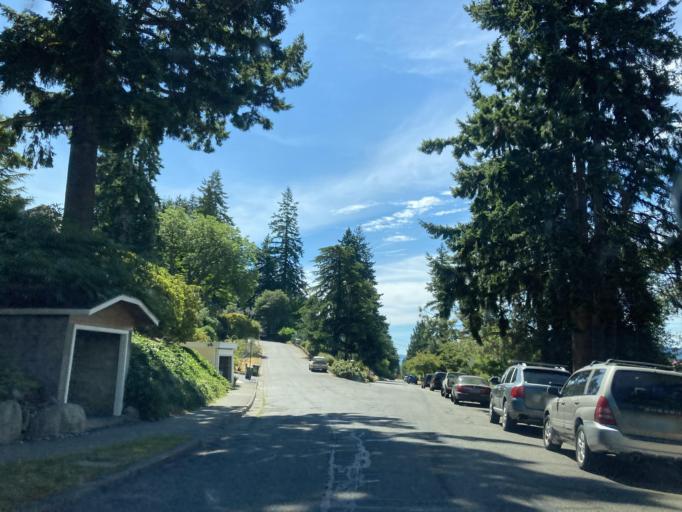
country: US
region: Washington
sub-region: Whatcom County
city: Bellingham
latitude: 48.7325
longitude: -122.4963
